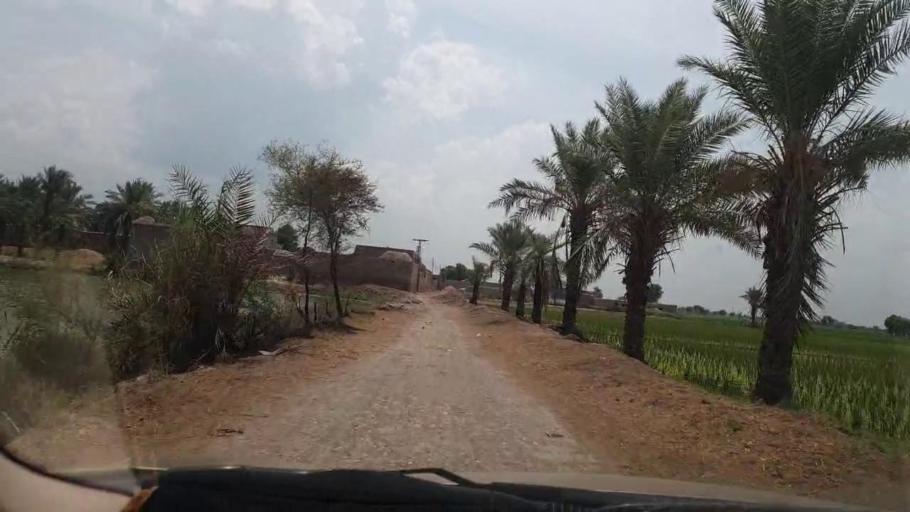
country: PK
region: Sindh
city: Larkana
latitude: 27.6146
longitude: 68.1500
